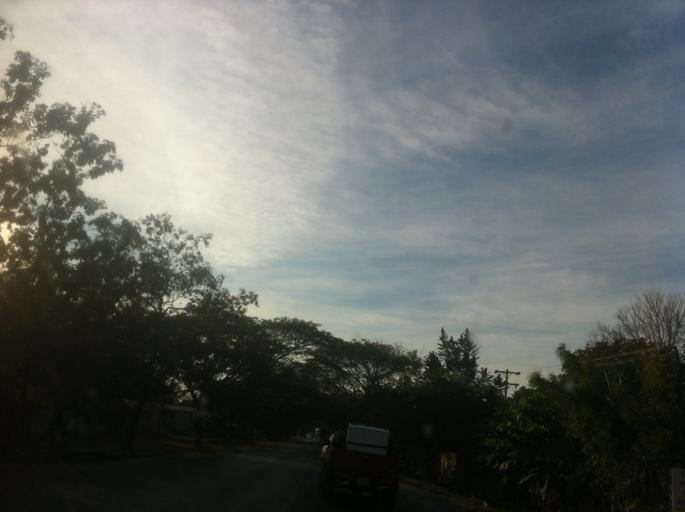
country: NI
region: Rivas
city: Rivas
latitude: 11.4152
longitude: -85.7947
